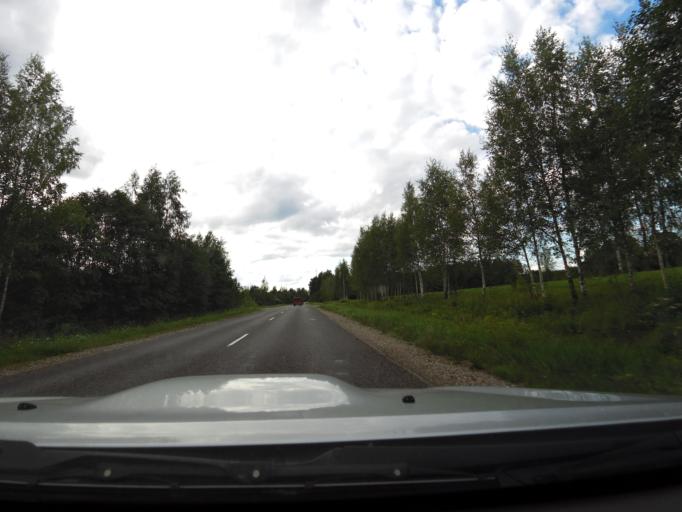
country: LV
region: Akniste
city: Akniste
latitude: 56.0092
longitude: 25.9368
